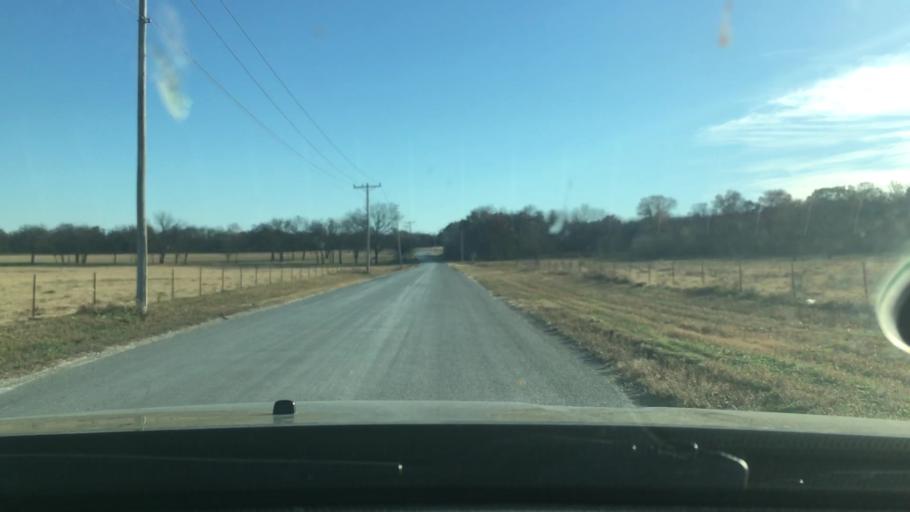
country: US
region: Oklahoma
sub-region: Murray County
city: Davis
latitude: 34.4947
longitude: -97.1580
